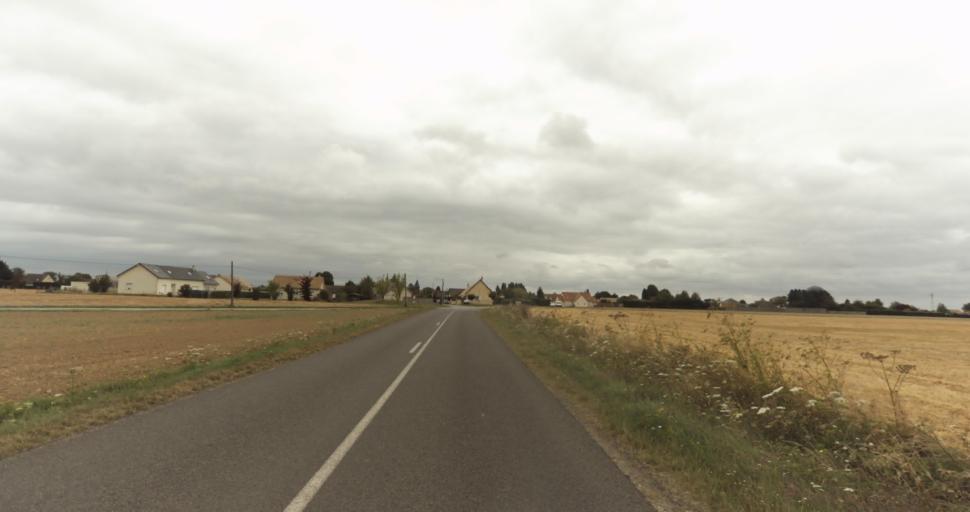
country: FR
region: Haute-Normandie
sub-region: Departement de l'Eure
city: Gravigny
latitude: 49.0357
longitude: 1.2397
